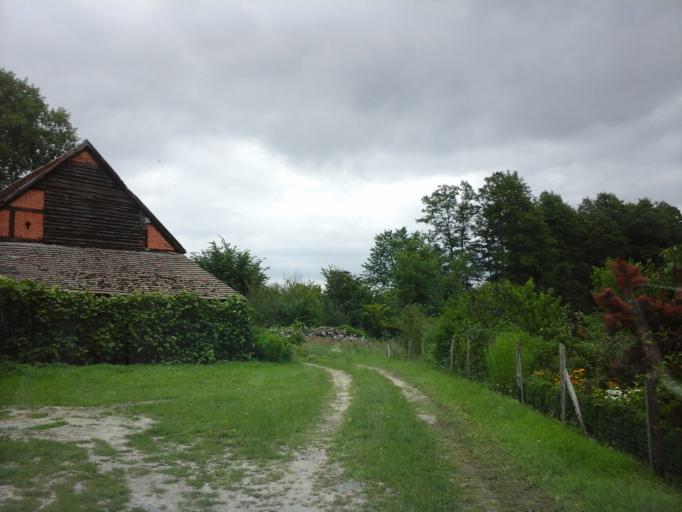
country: PL
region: West Pomeranian Voivodeship
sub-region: Powiat choszczenski
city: Krzecin
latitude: 53.0804
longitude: 15.4675
